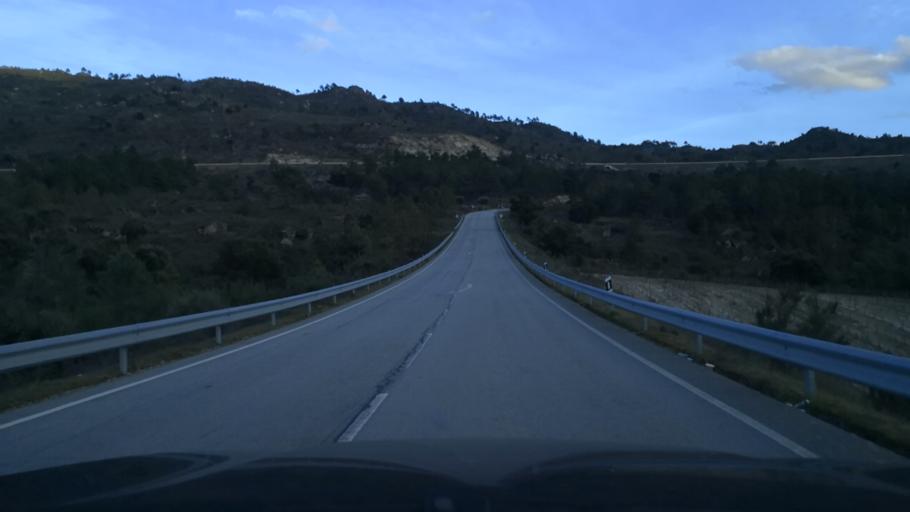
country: PT
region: Braganca
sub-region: Carrazeda de Ansiaes
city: Carrazeda de Anciaes
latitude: 41.2937
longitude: -7.3398
